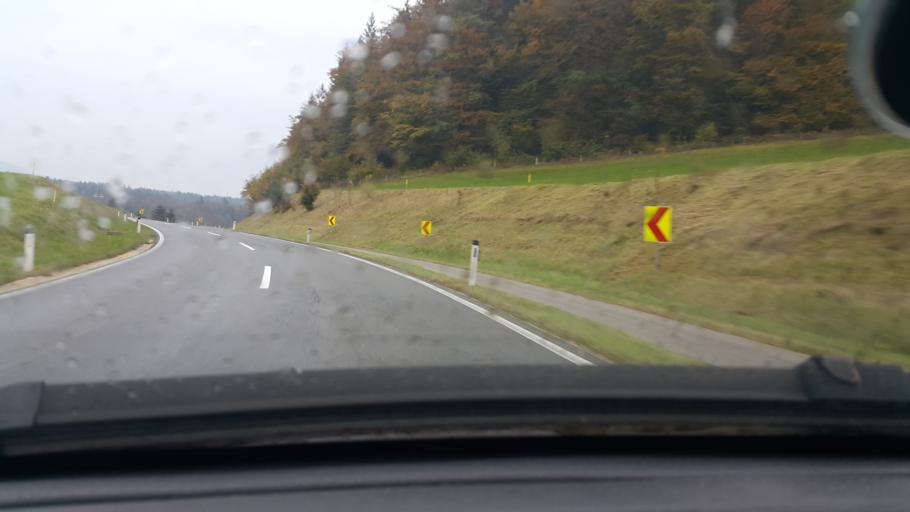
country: AT
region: Carinthia
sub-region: Politischer Bezirk Volkermarkt
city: Ruden
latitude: 46.6380
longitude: 14.7865
